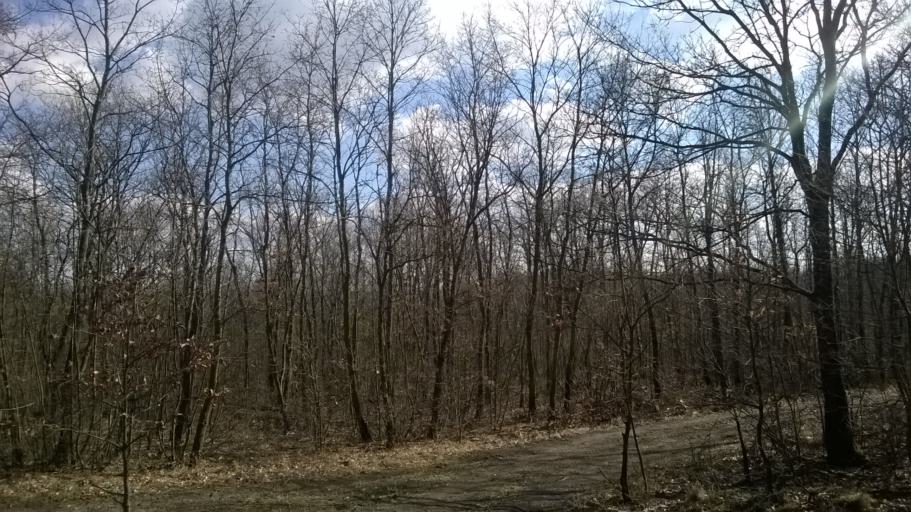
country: HU
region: Pest
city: Leanyfalu
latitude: 47.7296
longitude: 19.0766
